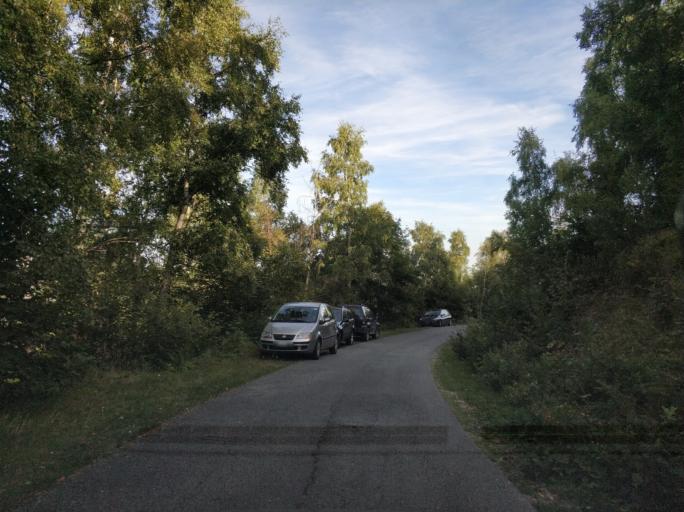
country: IT
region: Piedmont
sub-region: Provincia di Torino
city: Monastero di Lanzo
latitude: 45.3253
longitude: 7.4203
